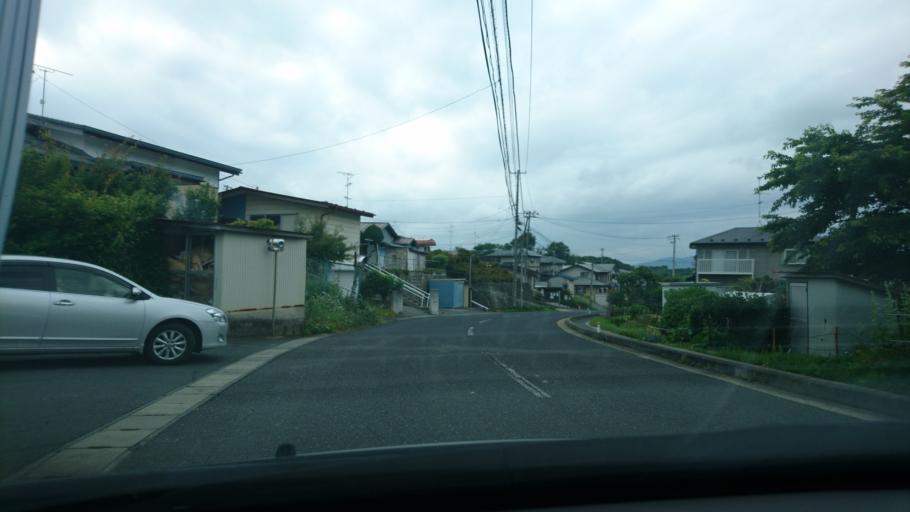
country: JP
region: Iwate
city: Ichinoseki
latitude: 38.9081
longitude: 141.1537
